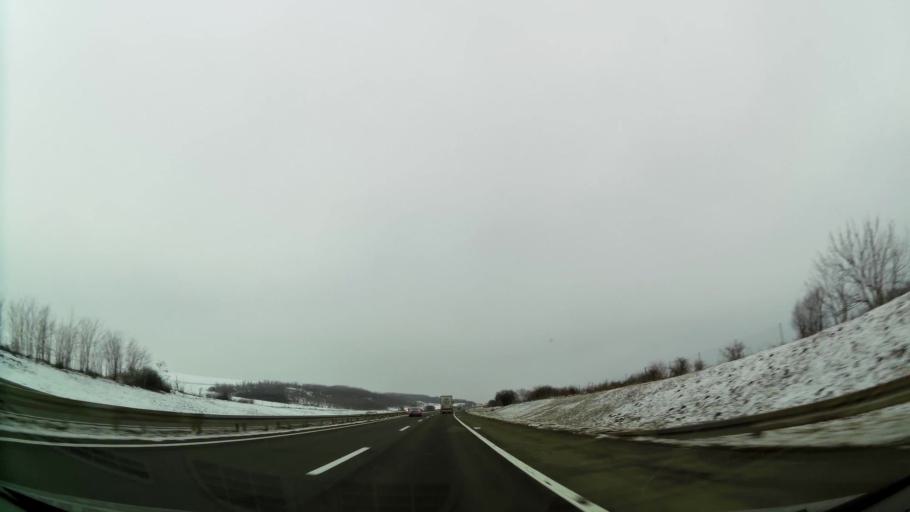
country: RS
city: Lugavcina
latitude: 44.5149
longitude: 21.0133
